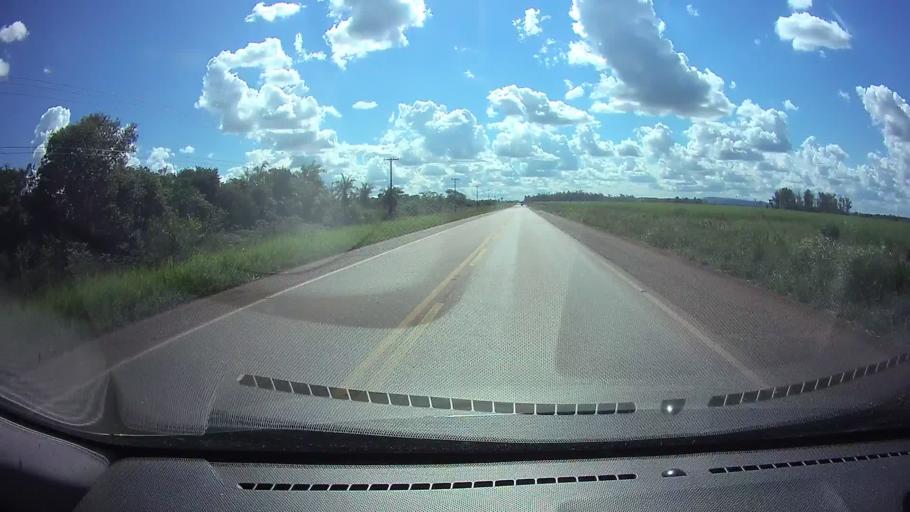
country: PY
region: Guaira
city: Coronel Martinez
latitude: -25.7587
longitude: -56.7528
